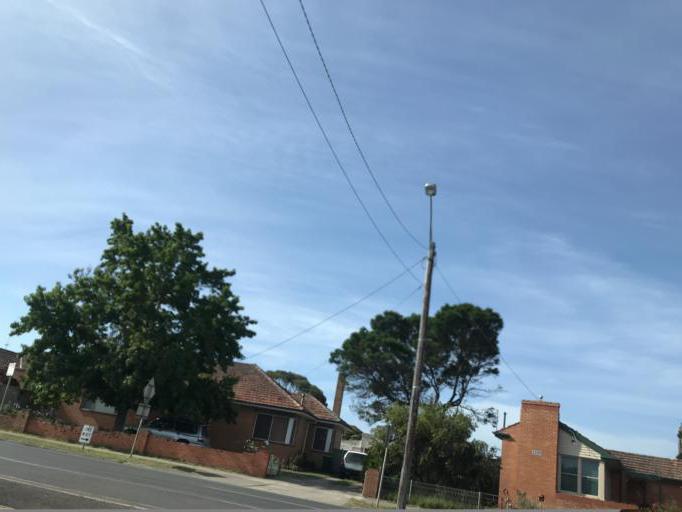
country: AU
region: Victoria
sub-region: Ballarat North
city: Newington
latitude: -37.5398
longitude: 143.8279
